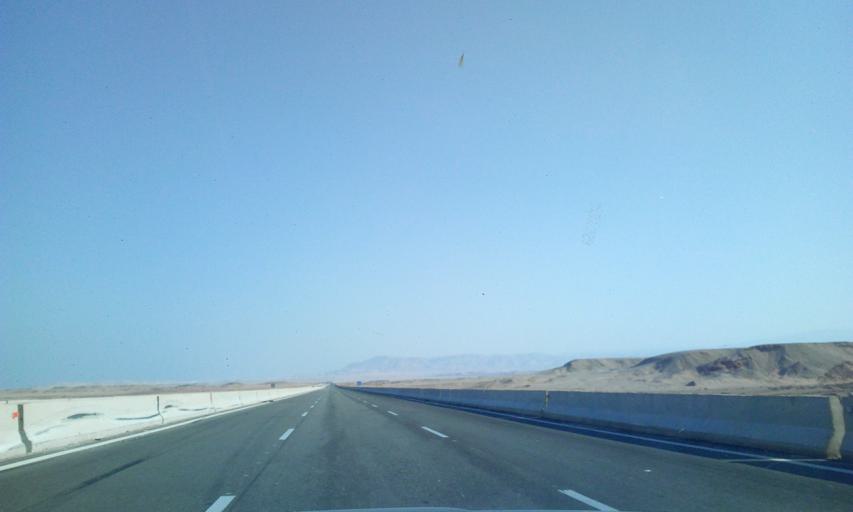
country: EG
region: As Suways
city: Ain Sukhna
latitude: 29.1602
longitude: 32.5114
